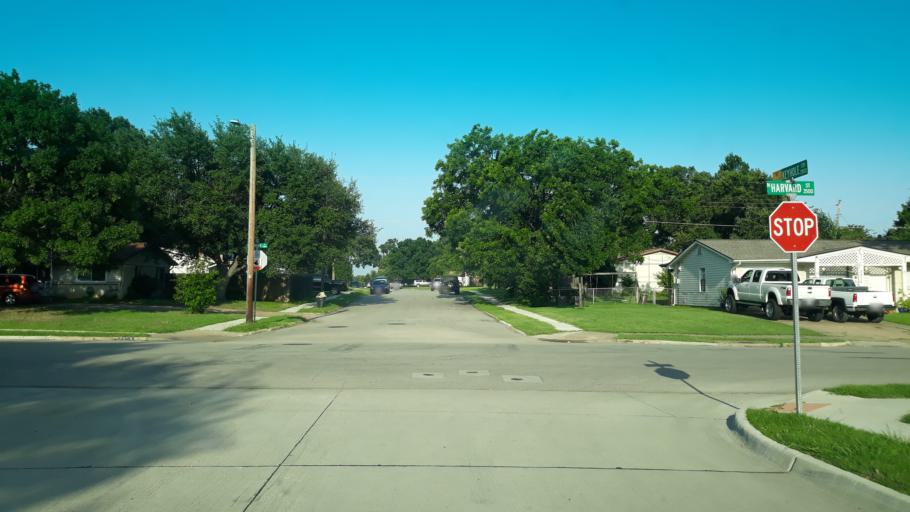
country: US
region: Texas
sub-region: Dallas County
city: Irving
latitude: 32.8541
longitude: -96.9857
